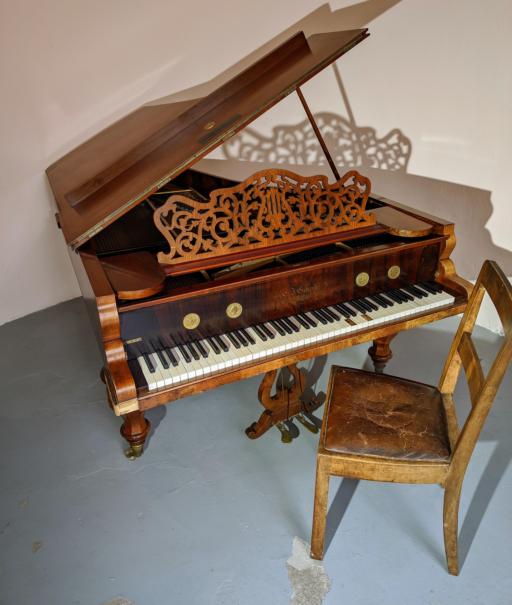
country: PL
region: Lower Silesian Voivodeship
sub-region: Powiat zabkowicki
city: Kamieniec Zabkowicki
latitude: 50.5206
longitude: 16.8814
